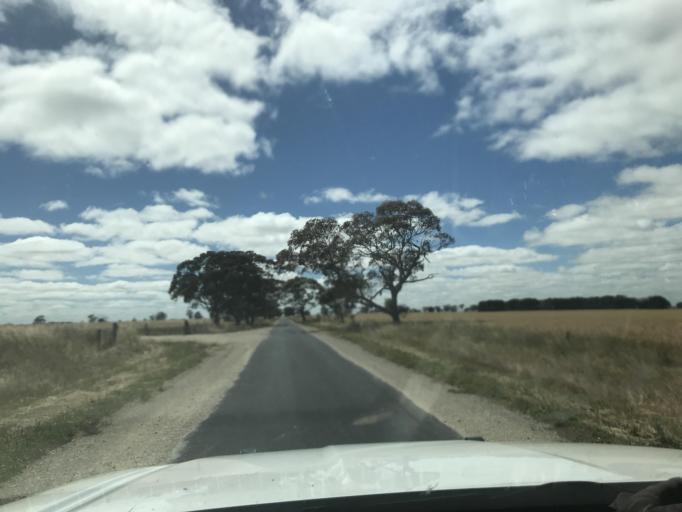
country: AU
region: South Australia
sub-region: Tatiara
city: Bordertown
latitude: -36.2786
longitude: 141.1164
